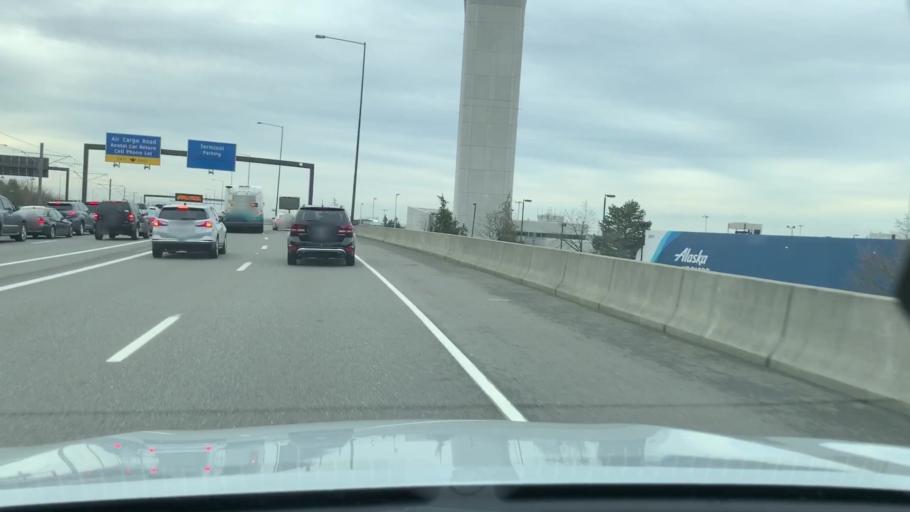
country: US
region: Washington
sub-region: King County
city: SeaTac
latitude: 47.4570
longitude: -122.3006
